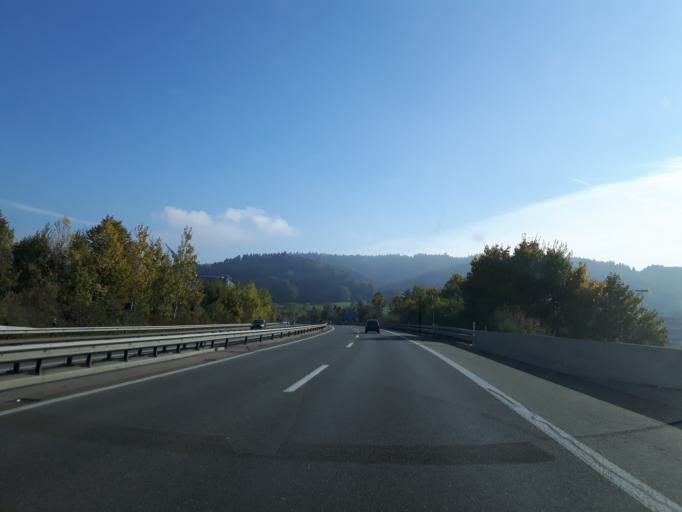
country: CH
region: Lucerne
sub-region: Willisau District
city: Dagmersellen
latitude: 47.2127
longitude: 7.9767
